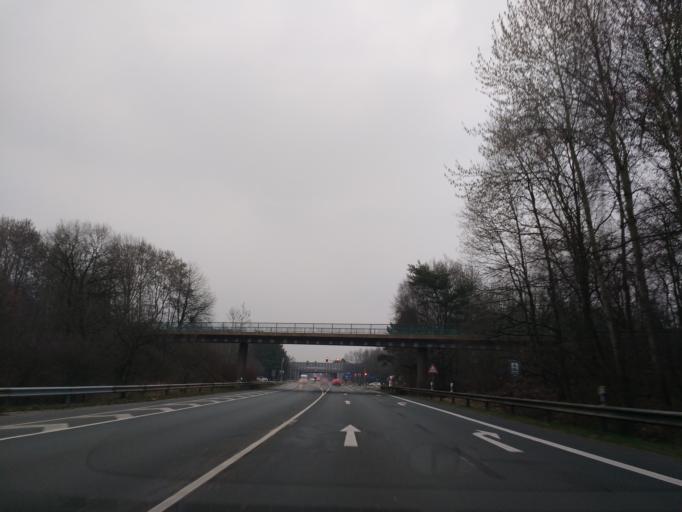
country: DE
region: North Rhine-Westphalia
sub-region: Regierungsbezirk Munster
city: Lotte
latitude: 52.3033
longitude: 7.9392
